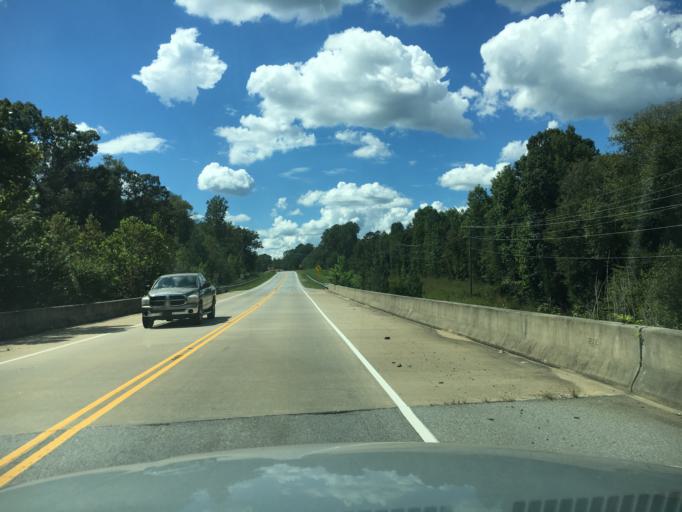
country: US
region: South Carolina
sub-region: Laurens County
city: Laurens
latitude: 34.5268
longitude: -82.1280
